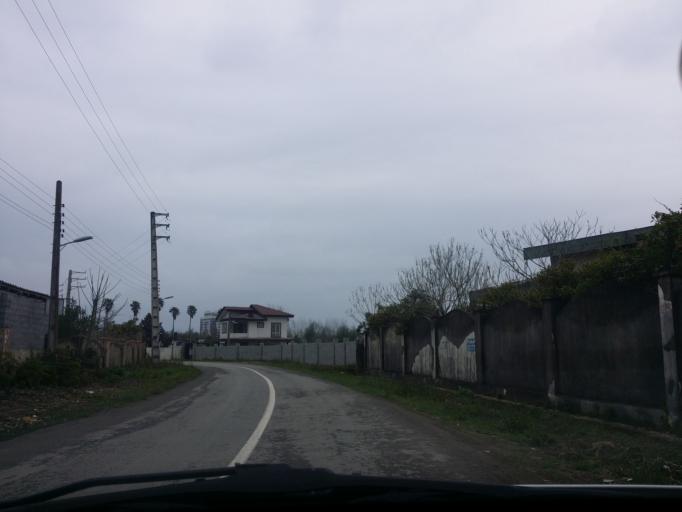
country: IR
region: Mazandaran
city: Chalus
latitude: 36.6809
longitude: 51.3791
